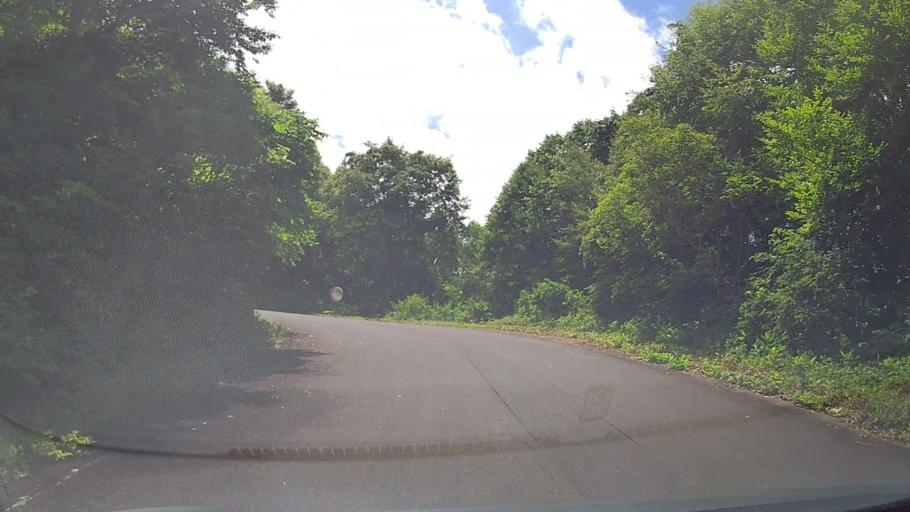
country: JP
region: Nagano
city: Iiyama
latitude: 36.9215
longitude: 138.4756
